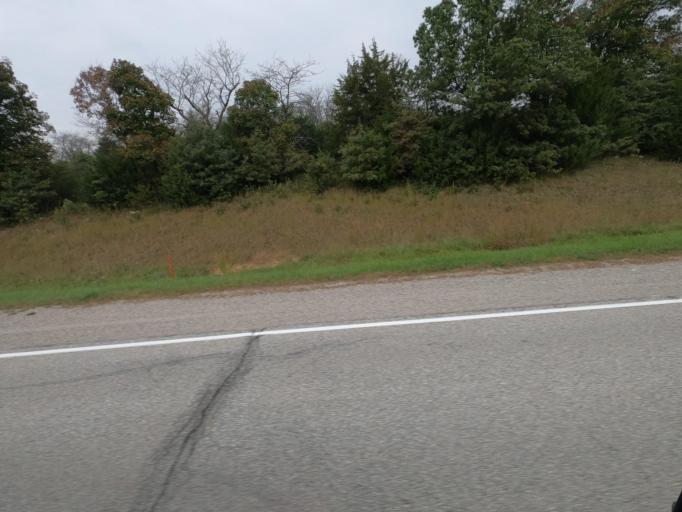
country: US
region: Iowa
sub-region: Van Buren County
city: Keosauqua
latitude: 40.8347
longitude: -91.9841
